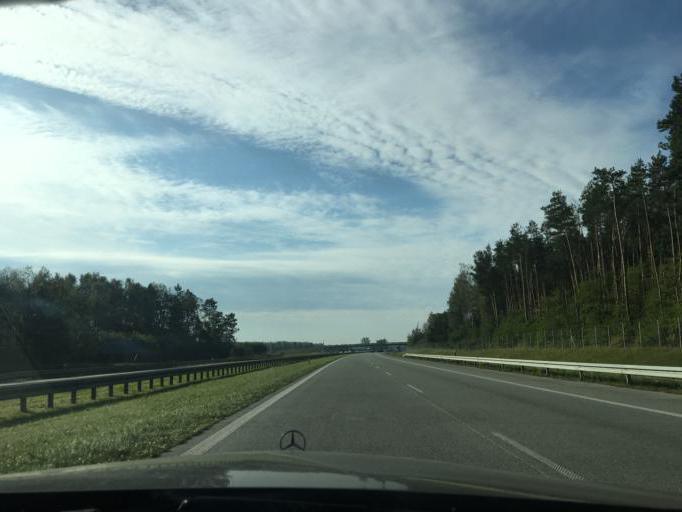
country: PL
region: Lodz Voivodeship
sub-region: Powiat lodzki wschodni
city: Andrespol
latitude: 51.7165
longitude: 19.6081
